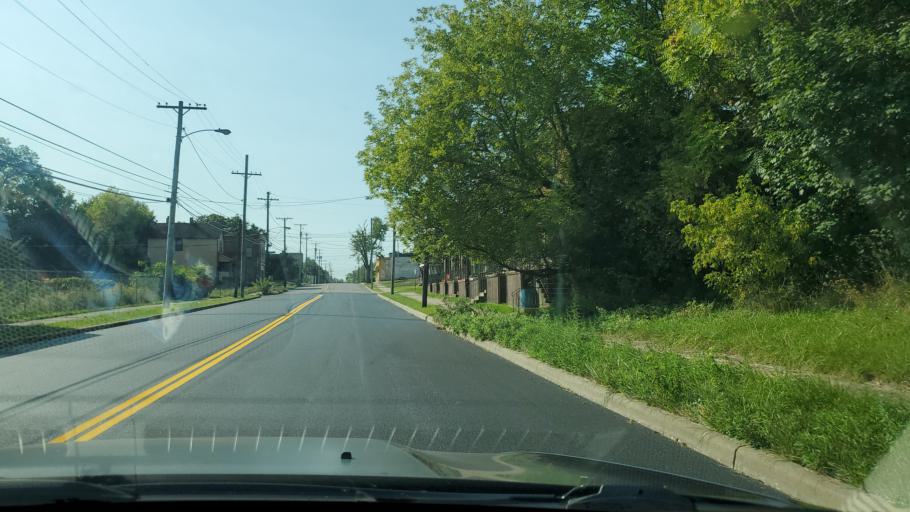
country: US
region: Ohio
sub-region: Mahoning County
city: Youngstown
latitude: 41.1116
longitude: -80.6828
